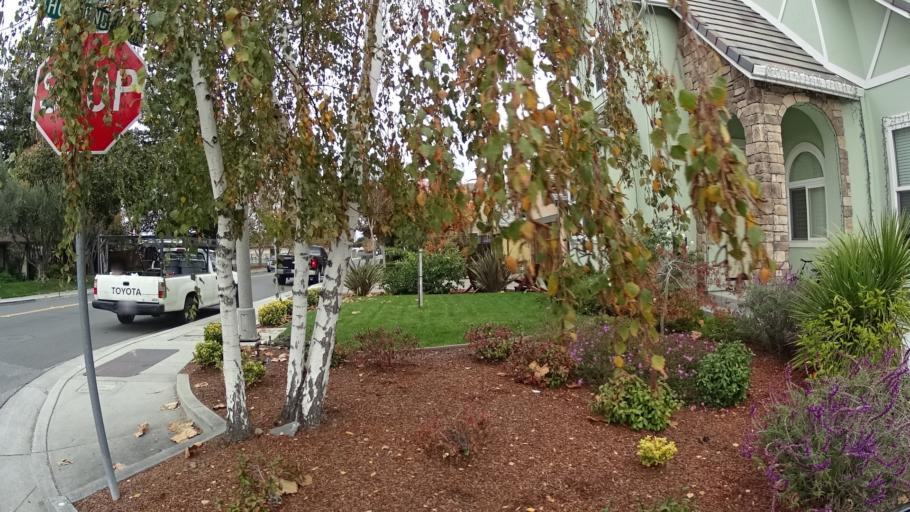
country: US
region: California
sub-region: Santa Clara County
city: Sunnyvale
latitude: 37.3536
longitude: -122.0414
